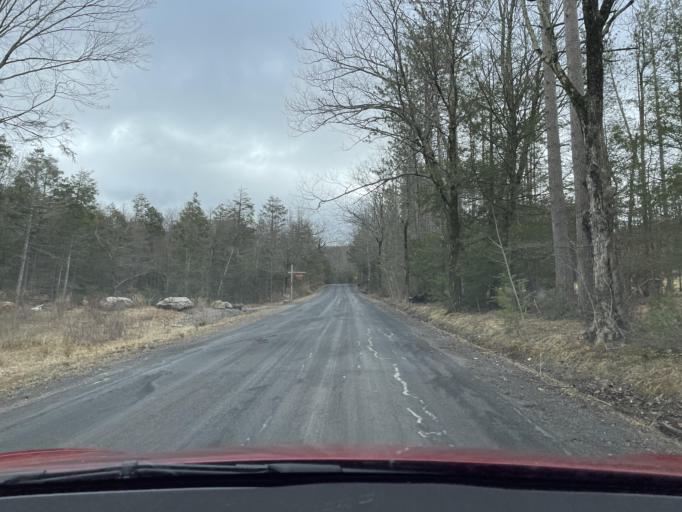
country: US
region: New York
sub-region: Ulster County
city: Woodstock
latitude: 42.0758
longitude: -74.1284
